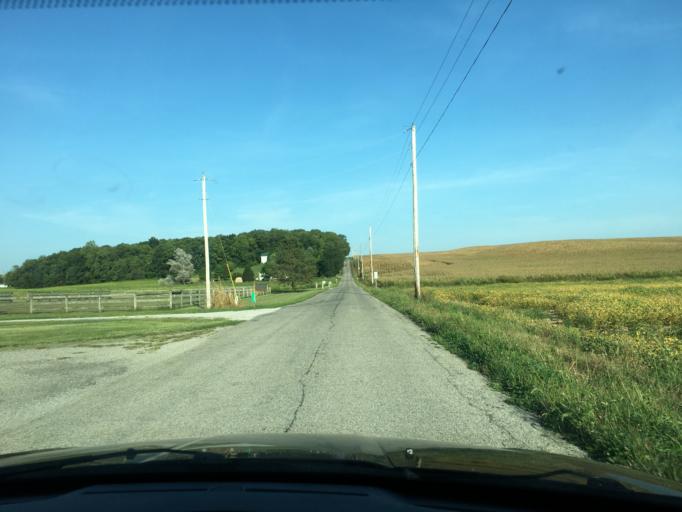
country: US
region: Ohio
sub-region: Logan County
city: West Liberty
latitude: 40.2991
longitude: -83.7411
